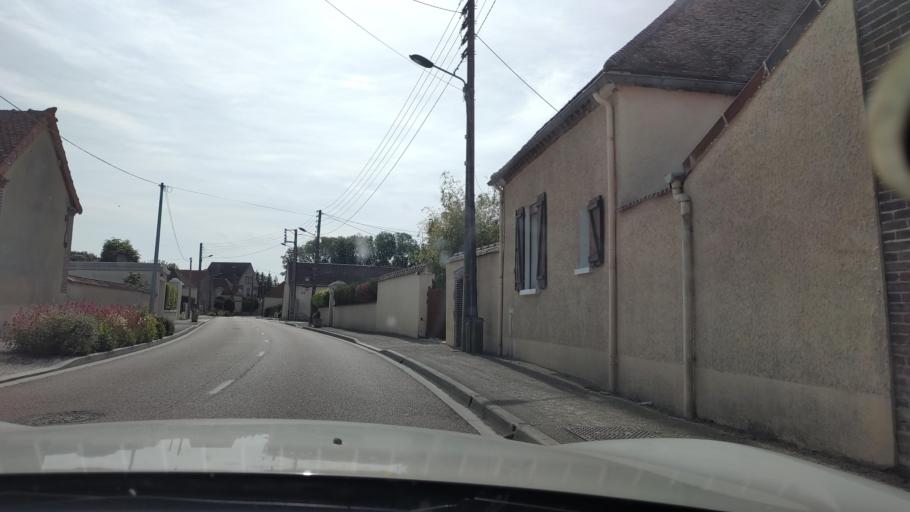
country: FR
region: Champagne-Ardenne
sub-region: Departement de l'Aube
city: Marigny-le-Chatel
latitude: 48.4041
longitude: 3.7316
